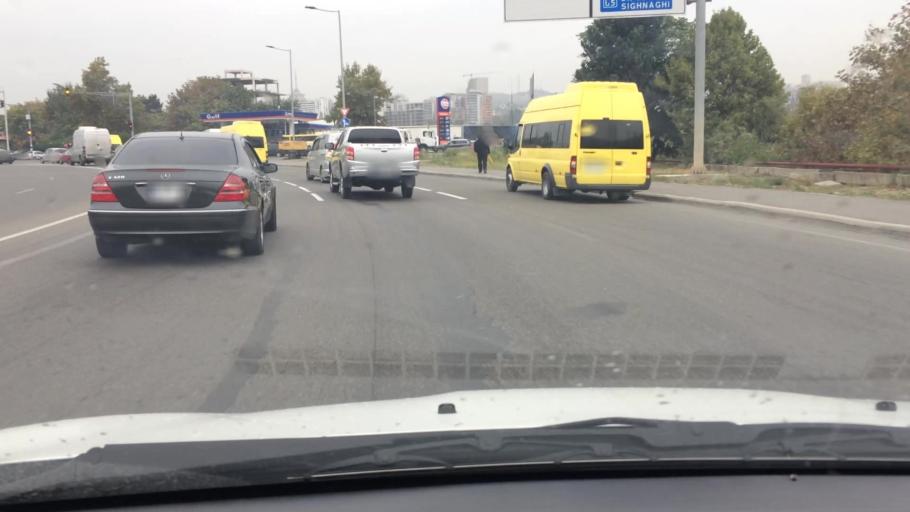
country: GE
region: T'bilisi
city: Tbilisi
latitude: 41.6754
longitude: 44.8364
